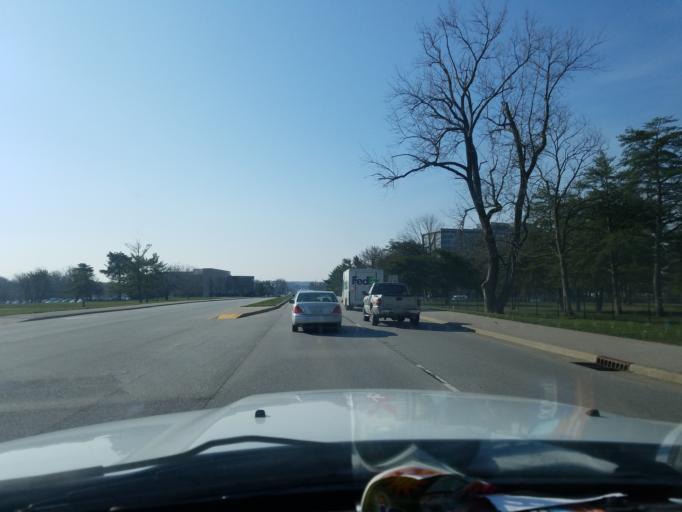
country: US
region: Indiana
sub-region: Monroe County
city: Bloomington
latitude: 39.1752
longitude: -86.5042
